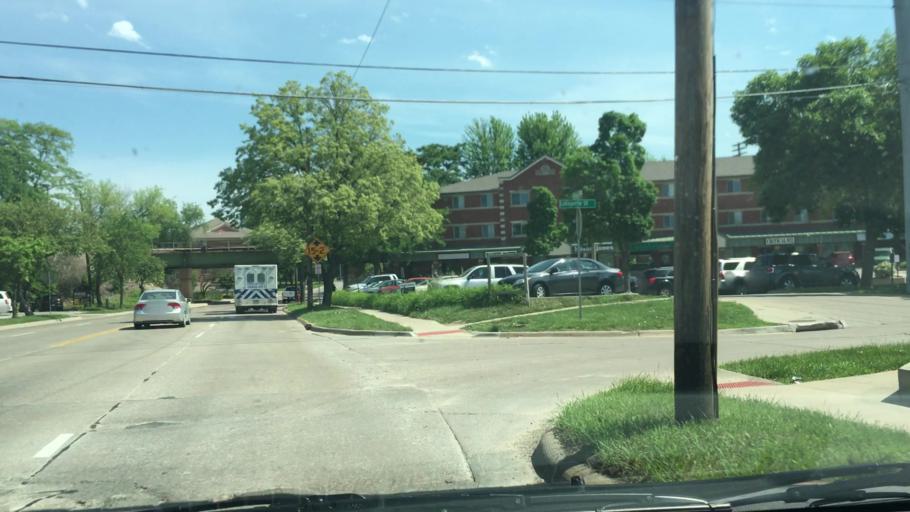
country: US
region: Iowa
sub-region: Johnson County
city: Iowa City
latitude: 41.6521
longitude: -91.5312
